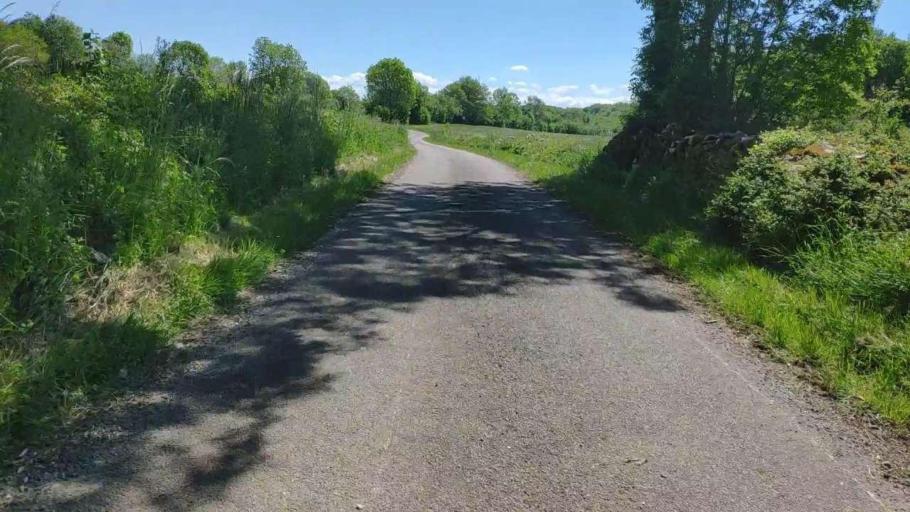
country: FR
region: Franche-Comte
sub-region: Departement du Jura
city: Perrigny
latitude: 46.7124
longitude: 5.6607
